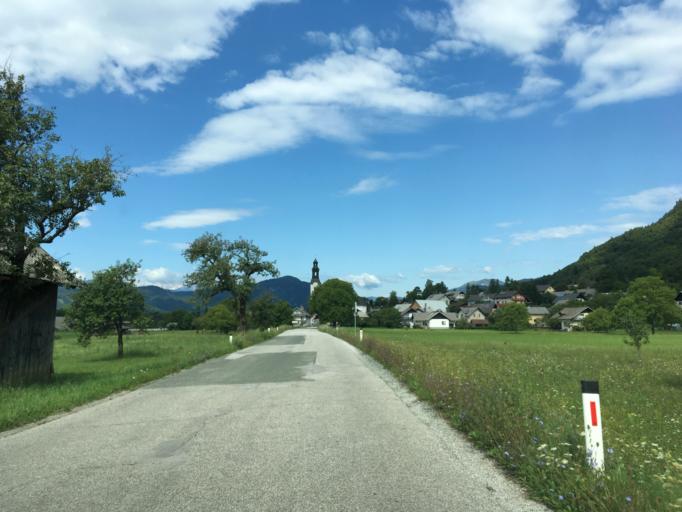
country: SI
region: Zirovnica
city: Zirovnica
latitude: 46.3940
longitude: 14.1582
